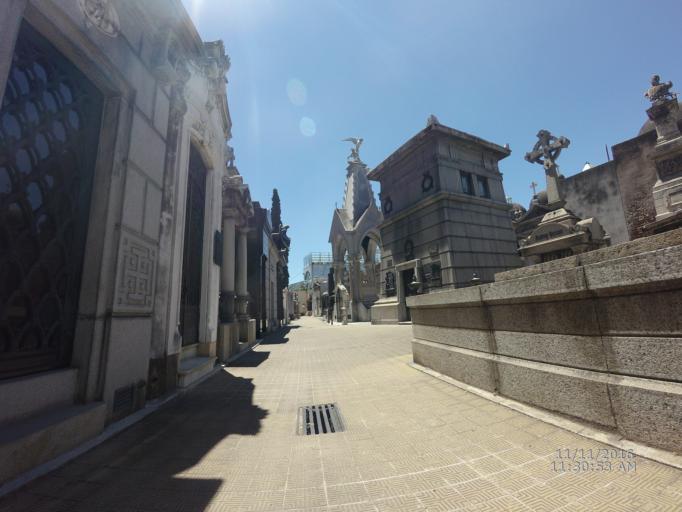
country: AR
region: Buenos Aires F.D.
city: Retiro
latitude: -34.5868
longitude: -58.3942
